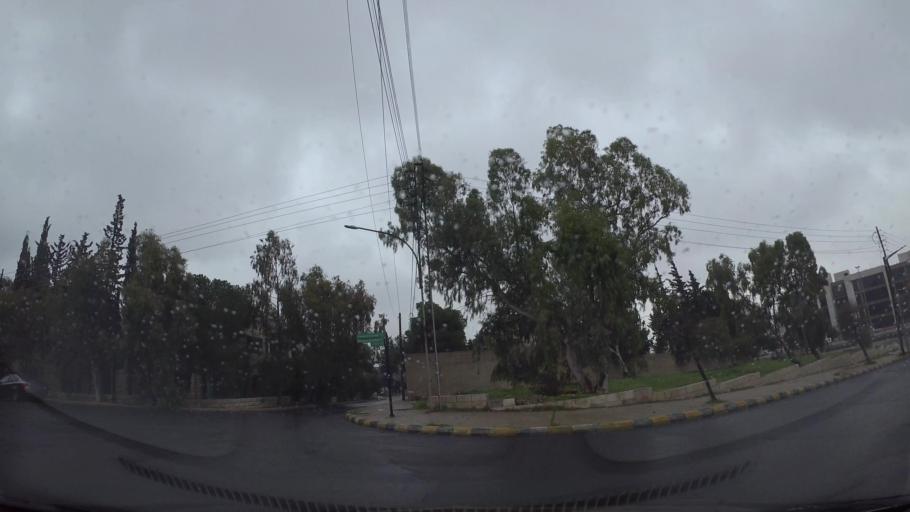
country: JO
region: Amman
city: Amman
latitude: 31.9567
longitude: 35.8977
